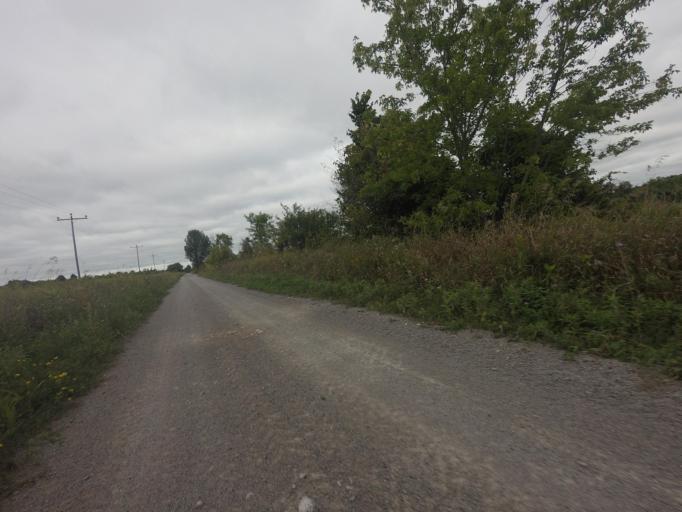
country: CA
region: Ontario
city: Omemee
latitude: 44.4561
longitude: -78.7616
